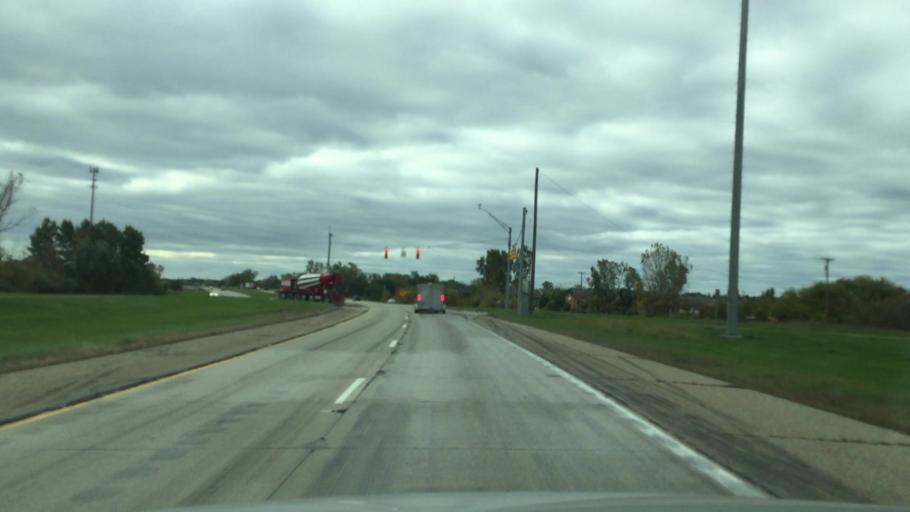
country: US
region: Michigan
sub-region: Macomb County
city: Shelby
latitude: 42.7341
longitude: -83.0263
